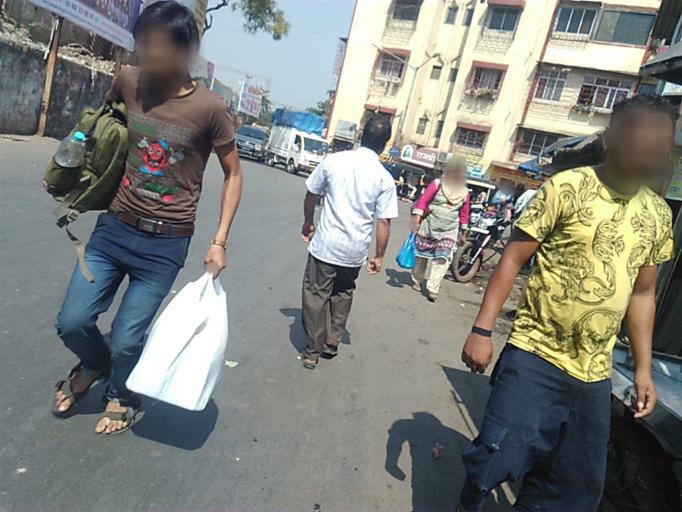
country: IN
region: Maharashtra
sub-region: Thane
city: Bhayandar
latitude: 19.3123
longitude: 72.8530
